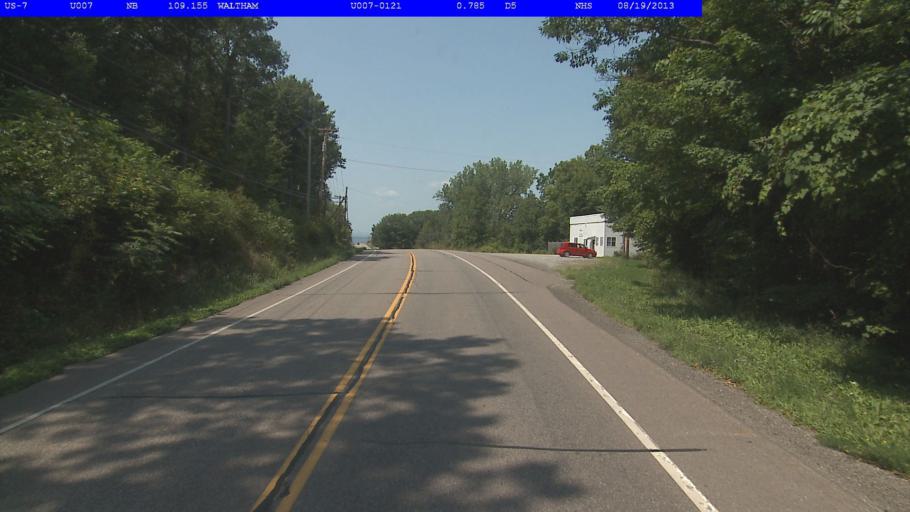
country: US
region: Vermont
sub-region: Addison County
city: Vergennes
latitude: 44.1561
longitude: -73.2207
